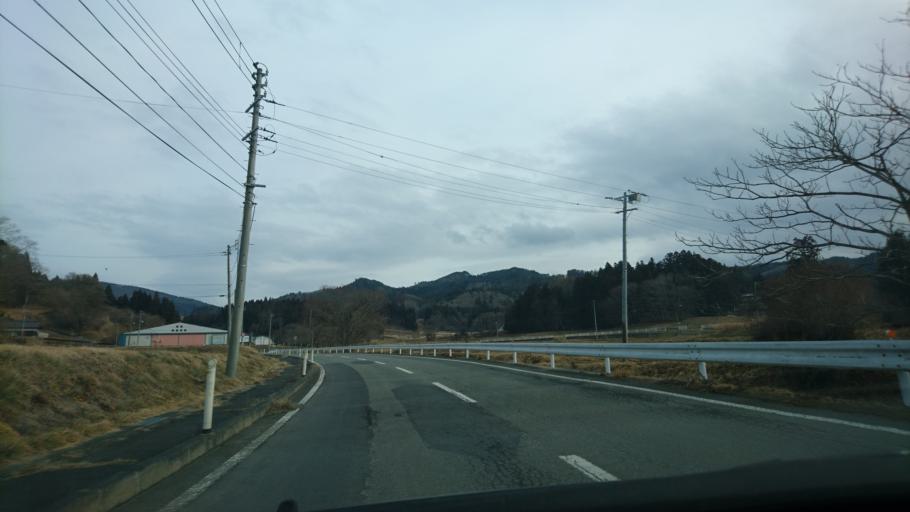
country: JP
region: Iwate
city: Ichinoseki
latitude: 38.8449
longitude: 141.3763
